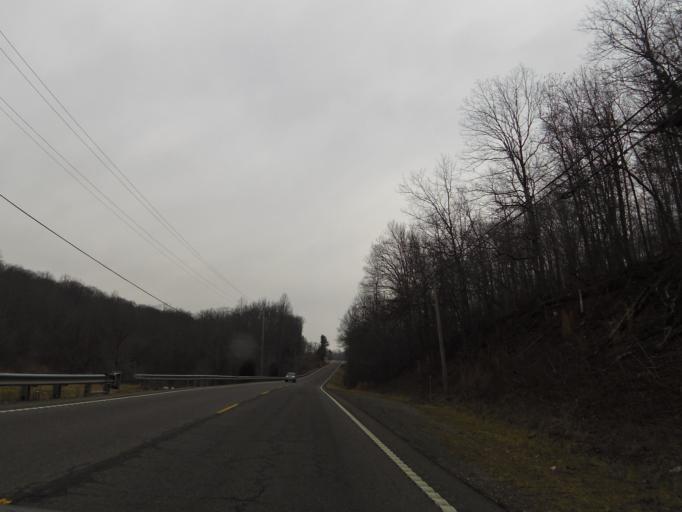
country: US
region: Tennessee
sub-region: Morgan County
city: Wartburg
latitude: 36.2079
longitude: -84.6619
